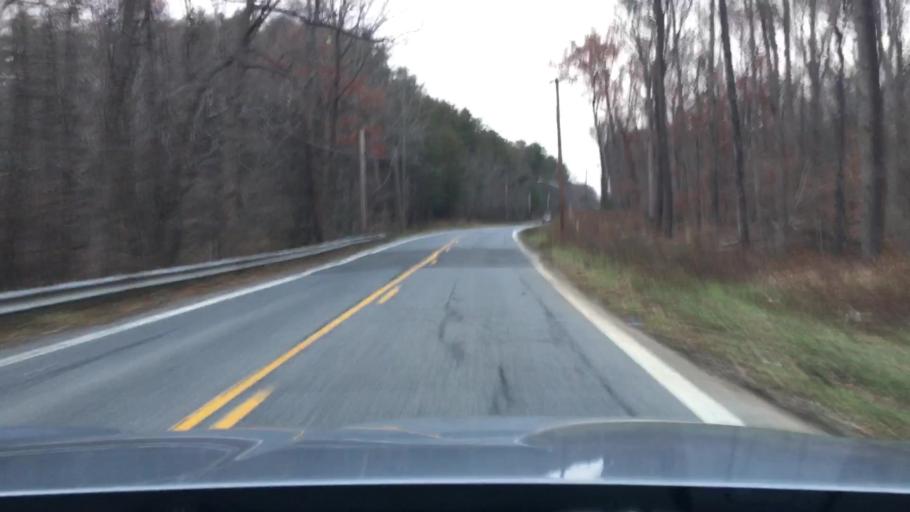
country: US
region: Maryland
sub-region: Prince George's County
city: Glenn Dale
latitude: 39.0244
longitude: -76.7860
